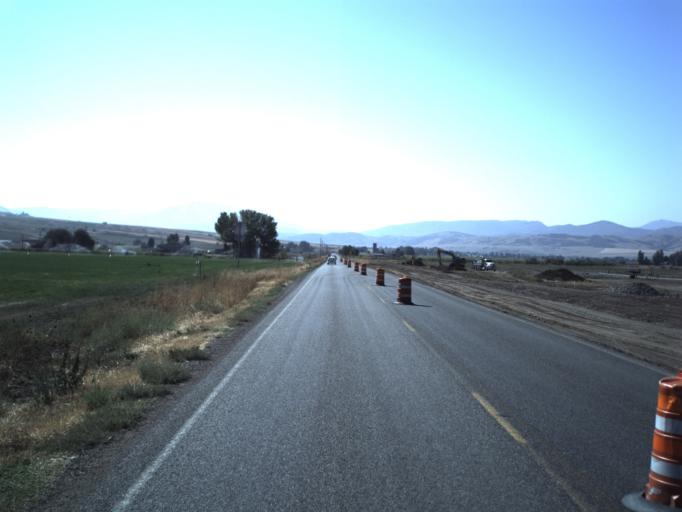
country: US
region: Utah
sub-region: Cache County
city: Hyrum
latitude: 41.6239
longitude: -111.8326
